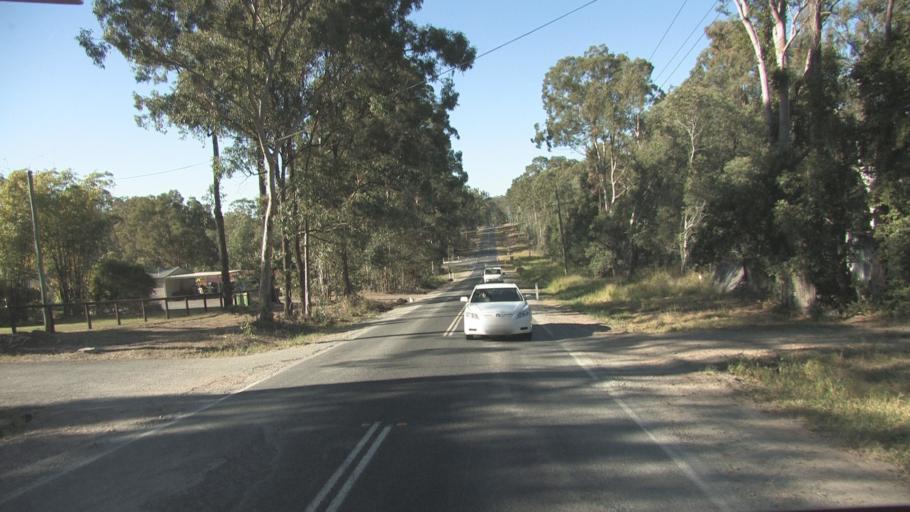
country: AU
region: Queensland
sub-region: Logan
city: Waterford West
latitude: -27.7415
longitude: 153.1441
